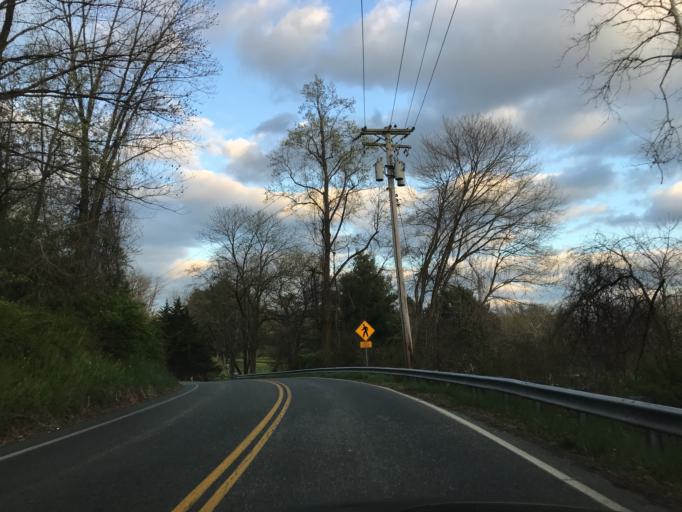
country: US
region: Maryland
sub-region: Harford County
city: Bel Air South
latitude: 39.5238
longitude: -76.3146
